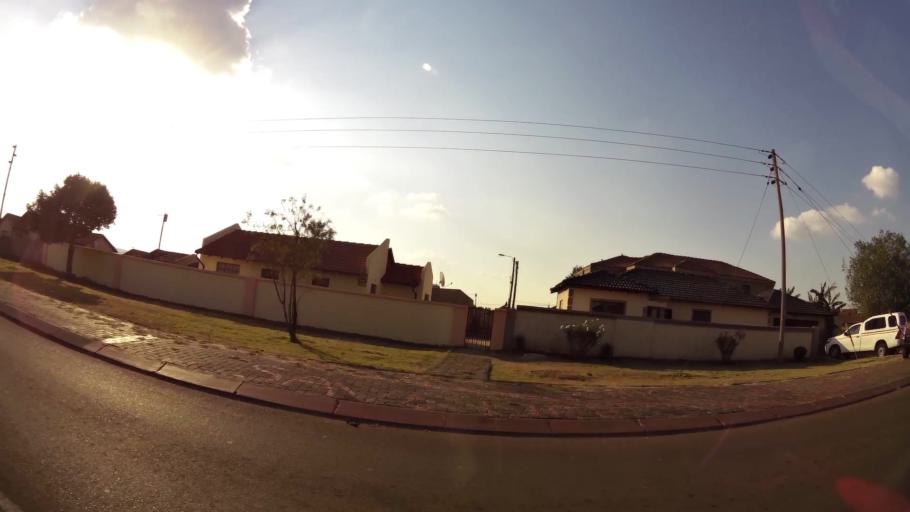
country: ZA
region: Gauteng
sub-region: Ekurhuleni Metropolitan Municipality
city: Tembisa
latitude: -25.9520
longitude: 28.2114
